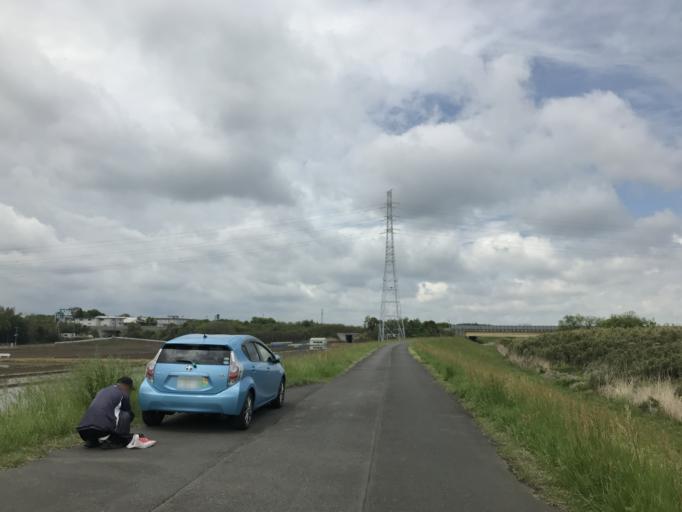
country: JP
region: Ibaraki
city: Mitsukaido
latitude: 35.9758
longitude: 139.9942
